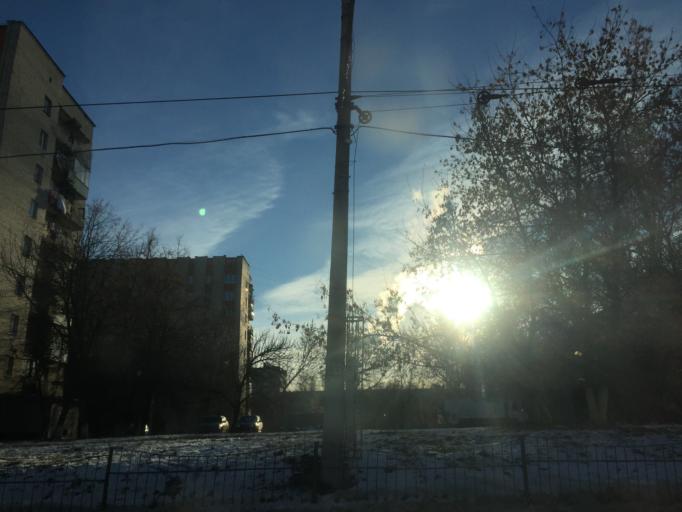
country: RU
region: Tula
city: Tula
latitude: 54.2193
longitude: 37.6152
